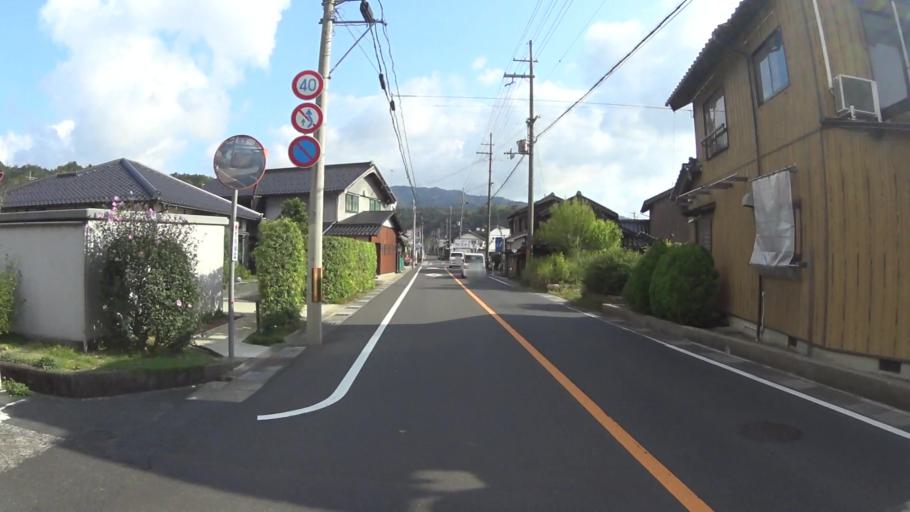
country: JP
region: Kyoto
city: Miyazu
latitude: 35.5697
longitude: 135.1555
